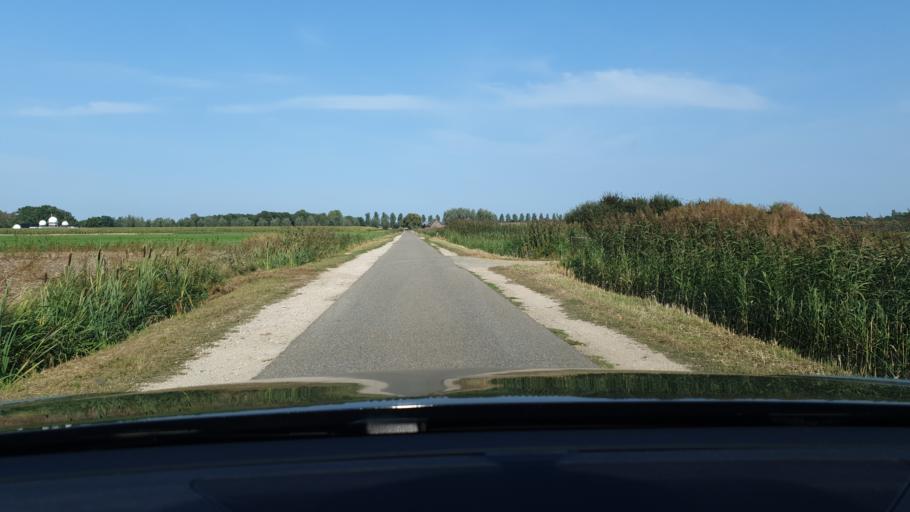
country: NL
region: North Brabant
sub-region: Gemeente Bernheze
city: Loosbroek
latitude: 51.6989
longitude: 5.4861
